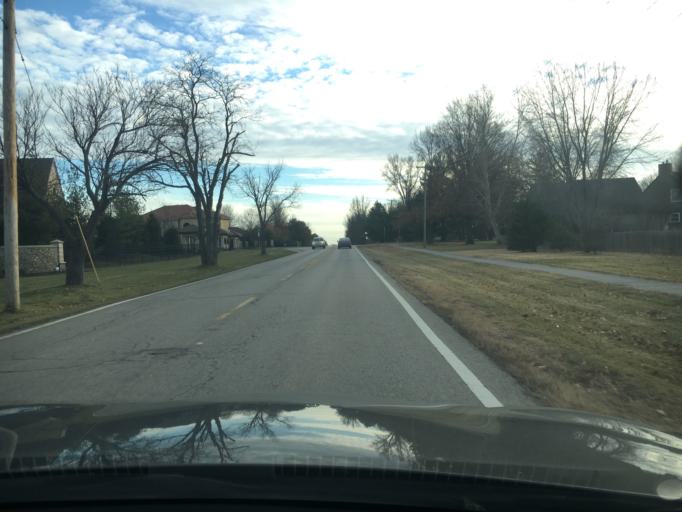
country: US
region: Kansas
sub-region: Johnson County
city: Leawood
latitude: 38.8767
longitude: -94.6306
